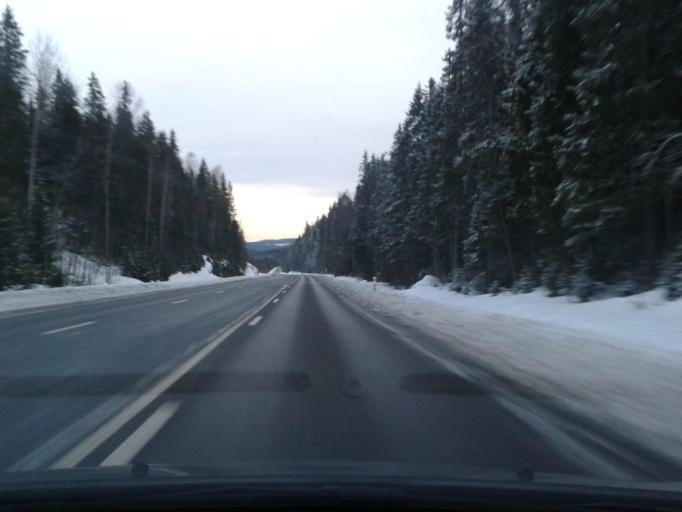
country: SE
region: Vaesternorrland
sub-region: Kramfors Kommun
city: Bollstabruk
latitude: 63.1150
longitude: 17.4954
